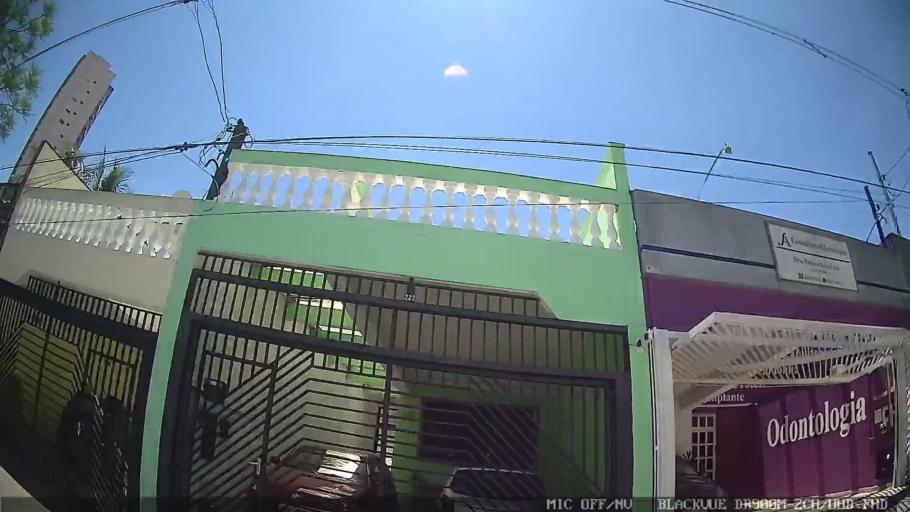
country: BR
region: Sao Paulo
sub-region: Sao Caetano Do Sul
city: Sao Caetano do Sul
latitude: -23.5909
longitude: -46.5690
